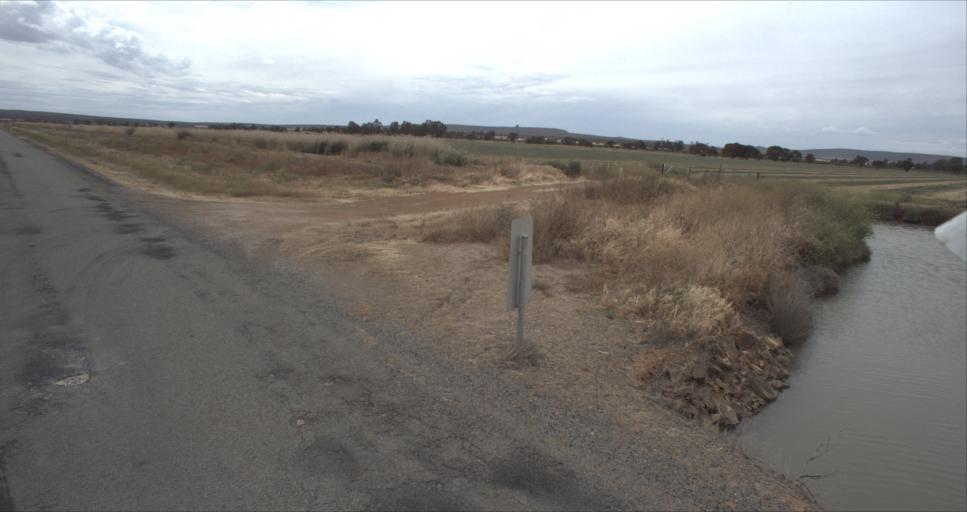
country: AU
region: New South Wales
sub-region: Leeton
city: Leeton
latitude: -34.4946
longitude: 146.4008
